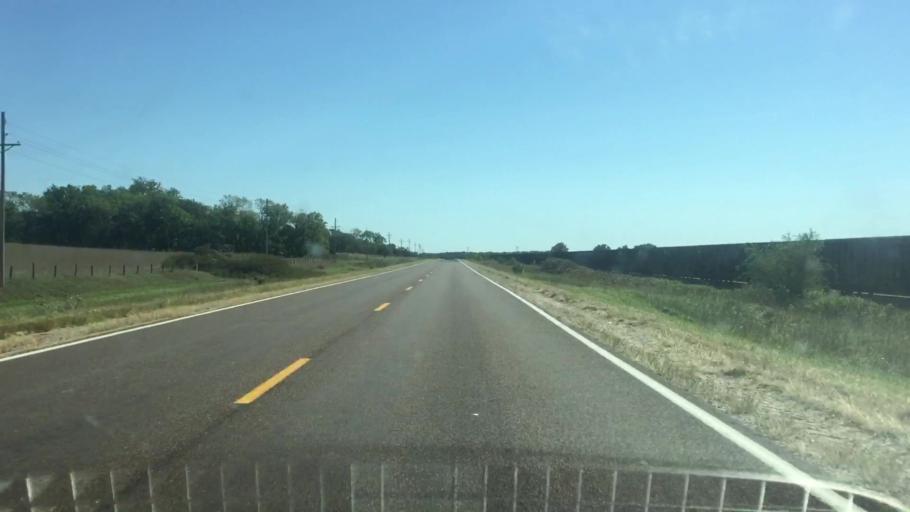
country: US
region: Nebraska
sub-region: Jefferson County
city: Fairbury
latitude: 40.0931
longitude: -97.1270
